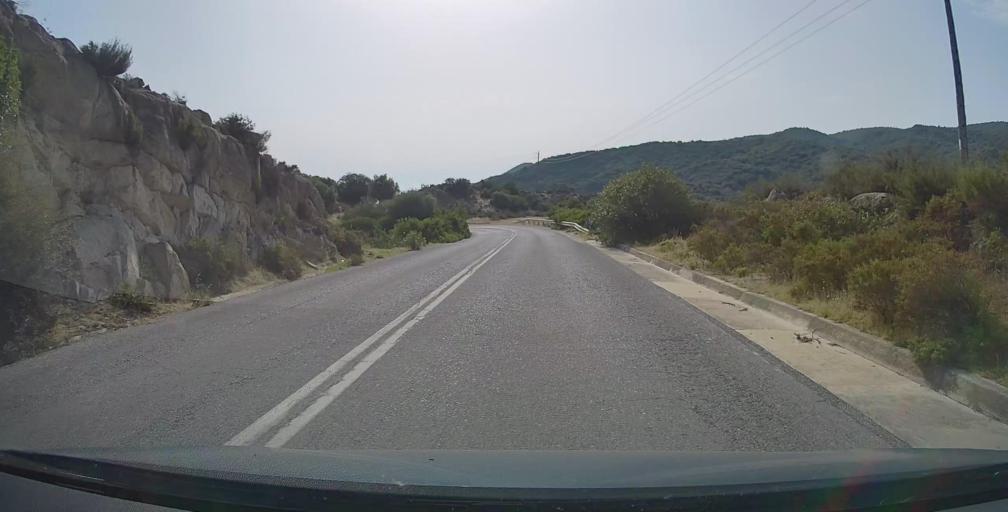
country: GR
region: Central Macedonia
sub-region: Nomos Chalkidikis
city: Sykia
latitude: 39.9885
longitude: 23.9719
